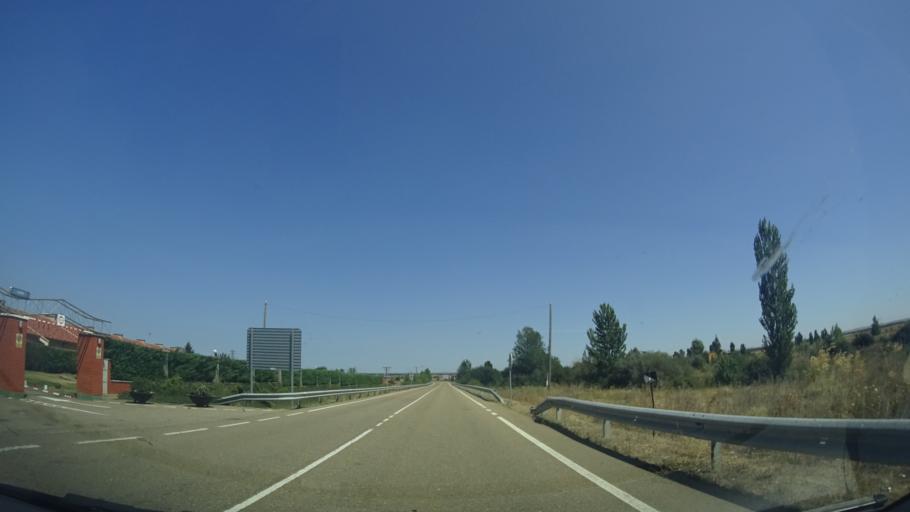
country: ES
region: Castille and Leon
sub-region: Provincia de Leon
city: Ardon
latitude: 42.4397
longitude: -5.5818
